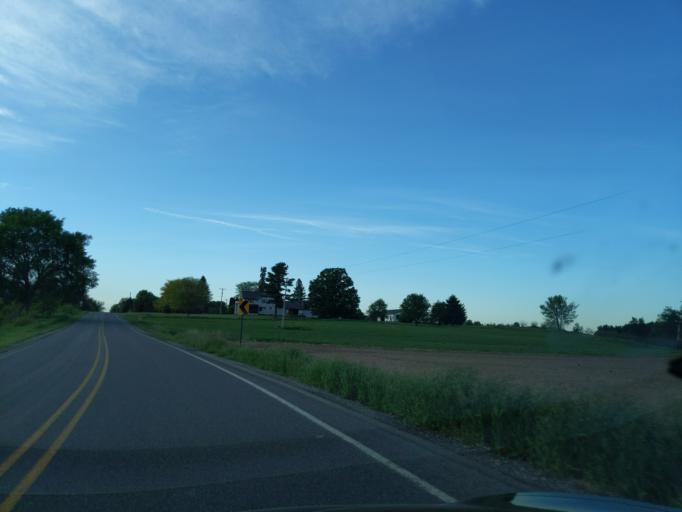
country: US
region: Michigan
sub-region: Ingham County
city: Williamston
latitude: 42.5657
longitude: -84.2983
